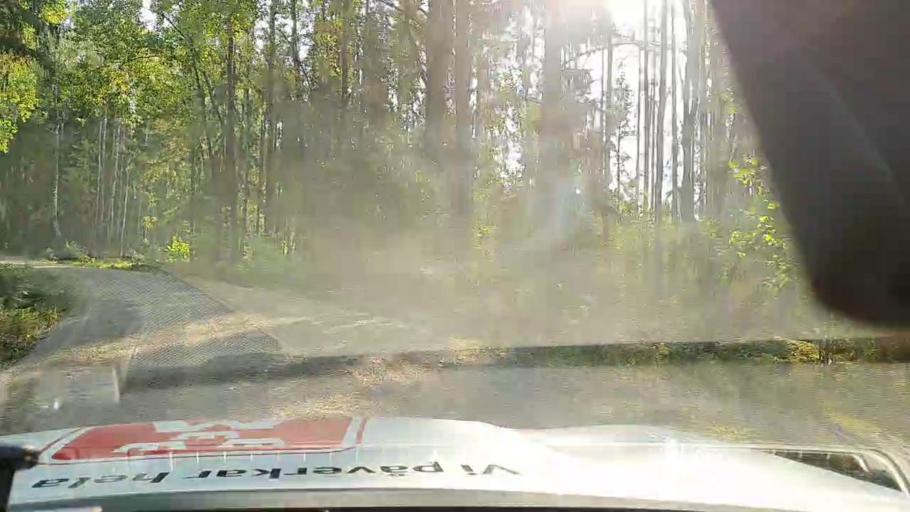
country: SE
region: Vaestmanland
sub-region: Kungsors Kommun
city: Kungsoer
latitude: 59.3474
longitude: 16.1684
